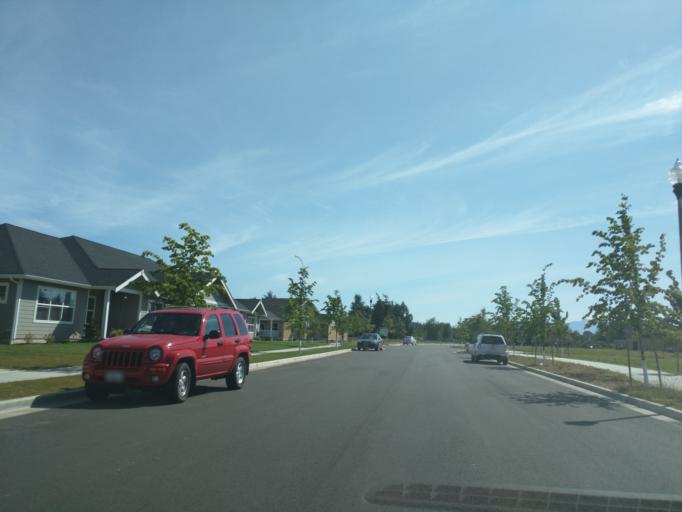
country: US
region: Washington
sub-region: Whatcom County
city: Lynden
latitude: 48.9620
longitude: -122.4134
